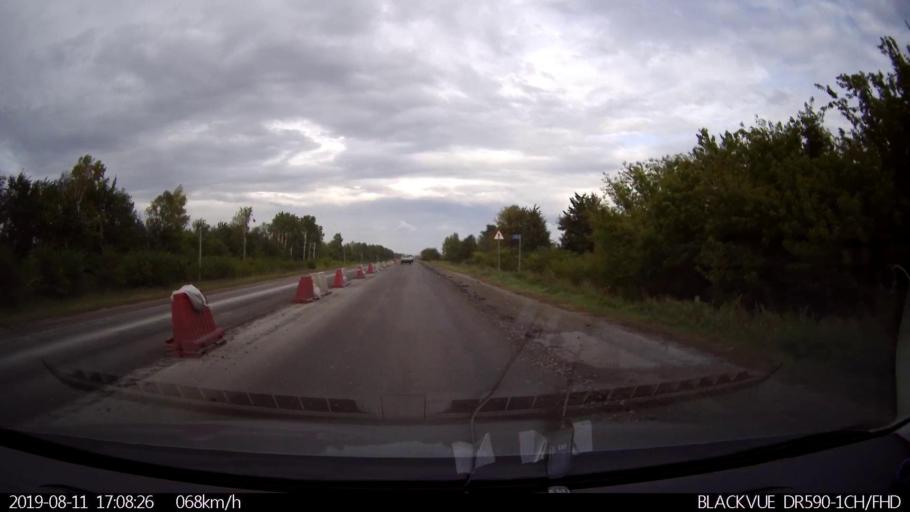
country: RU
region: Ulyanovsk
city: Mayna
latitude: 54.2926
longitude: 47.8391
